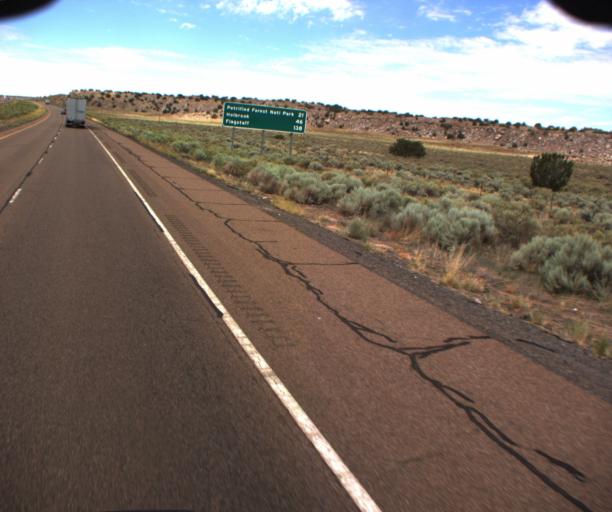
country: US
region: Arizona
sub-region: Apache County
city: Houck
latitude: 35.1859
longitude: -109.4507
